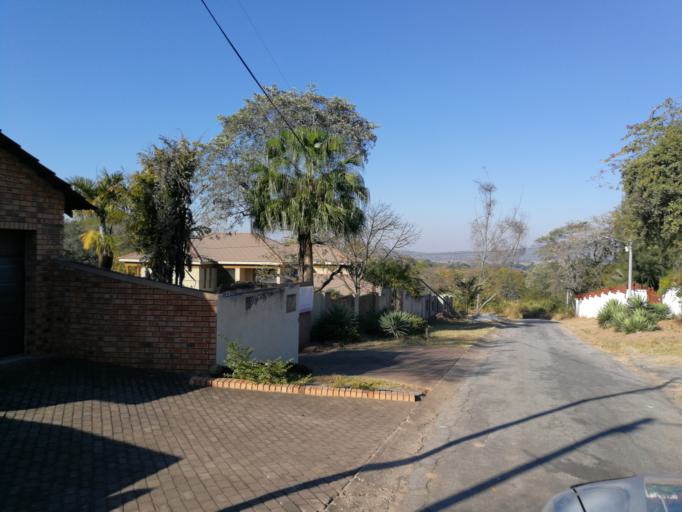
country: ZA
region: Mpumalanga
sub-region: Ehlanzeni District
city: White River
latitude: -25.0662
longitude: 31.1125
